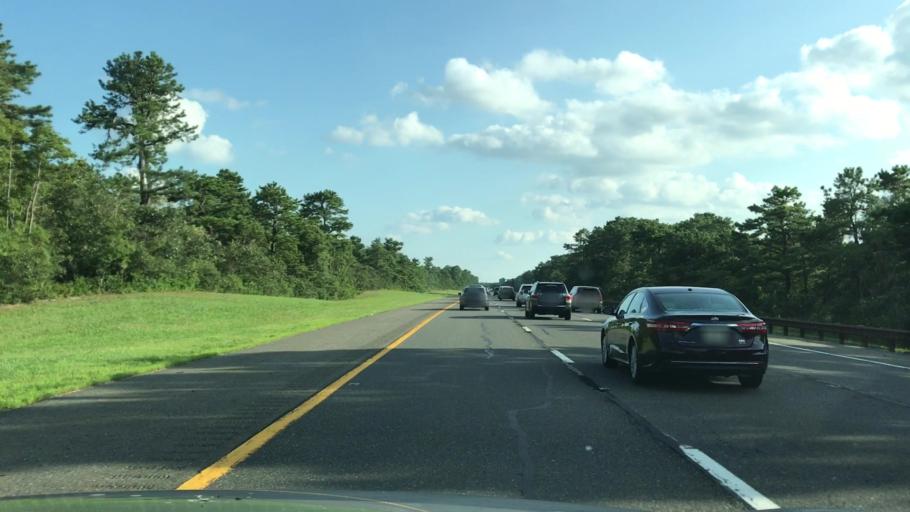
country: US
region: New Jersey
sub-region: Ocean County
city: Waretown
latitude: 39.8138
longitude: -74.2307
